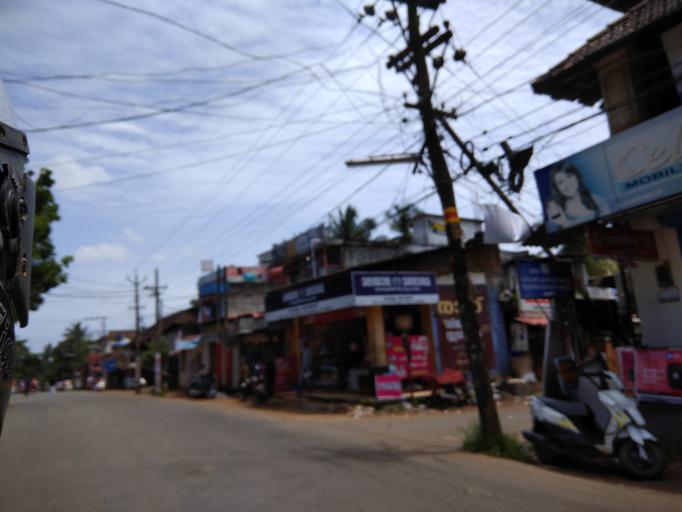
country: IN
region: Kerala
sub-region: Thrissur District
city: Trichur
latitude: 10.4977
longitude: 76.1593
